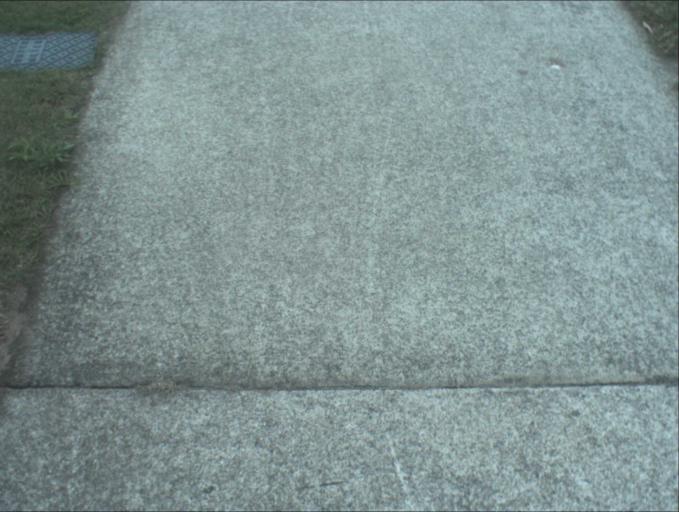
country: AU
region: Queensland
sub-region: Logan
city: Park Ridge South
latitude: -27.6865
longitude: 153.0314
